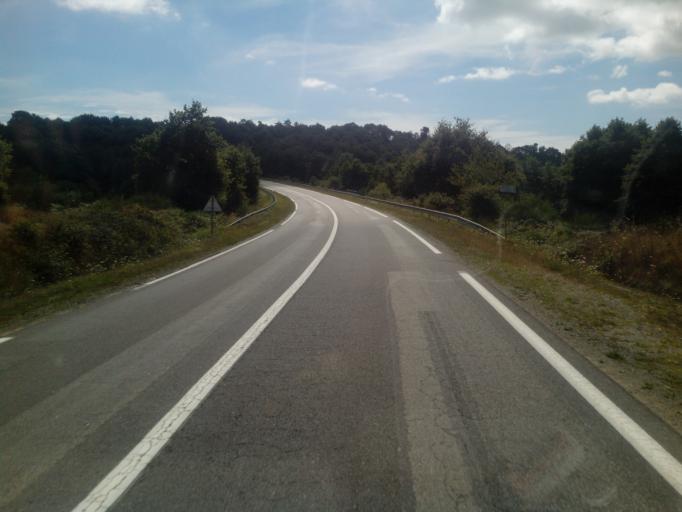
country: FR
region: Brittany
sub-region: Departement du Morbihan
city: Peaule
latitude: 47.5656
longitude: -2.3928
